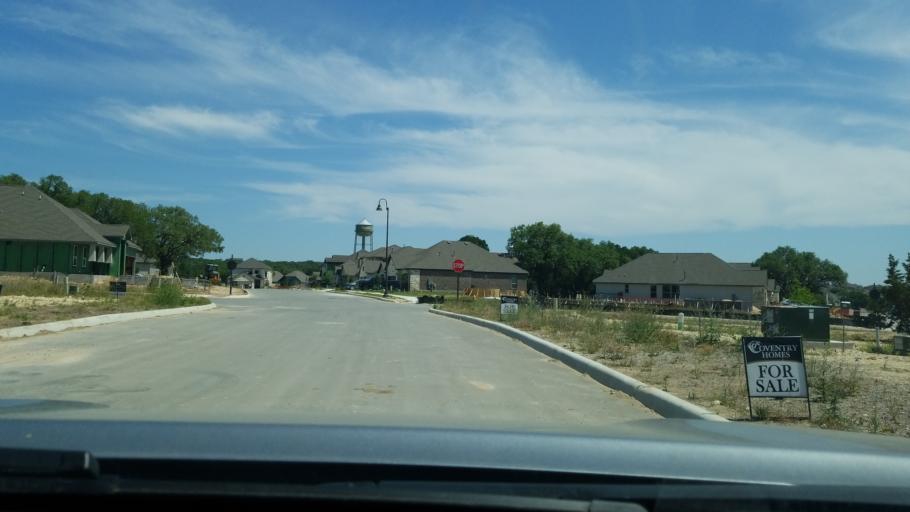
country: US
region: Texas
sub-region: Kendall County
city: Boerne
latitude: 29.8022
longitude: -98.6950
